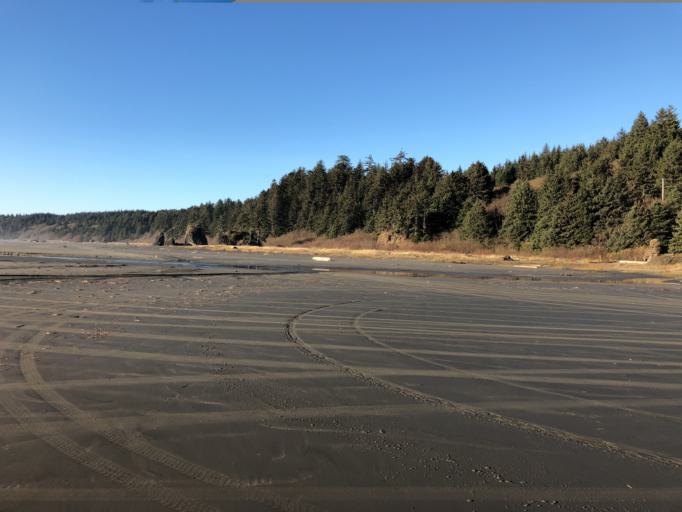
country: US
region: Washington
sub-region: Grays Harbor County
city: Ocean Shores
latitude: 47.2982
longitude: -124.2480
